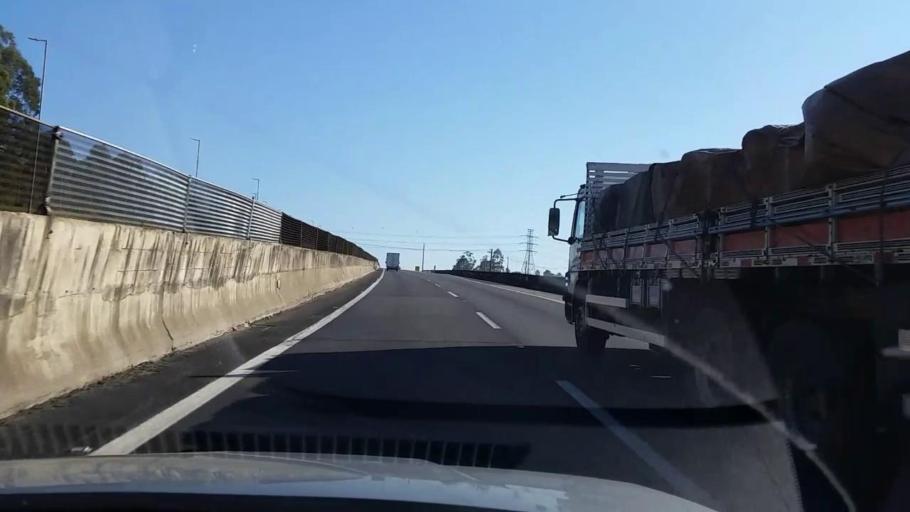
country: BR
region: Sao Paulo
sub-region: Varzea Paulista
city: Varzea Paulista
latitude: -23.2372
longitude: -46.8698
